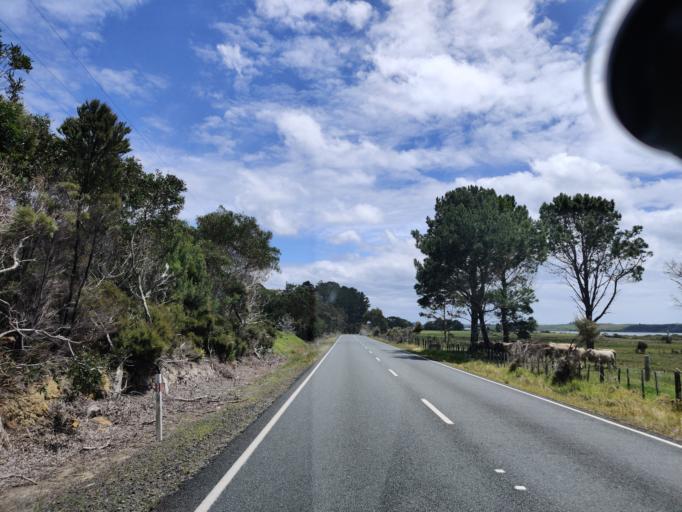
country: NZ
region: Northland
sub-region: Far North District
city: Kaitaia
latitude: -34.8015
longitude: 173.1101
